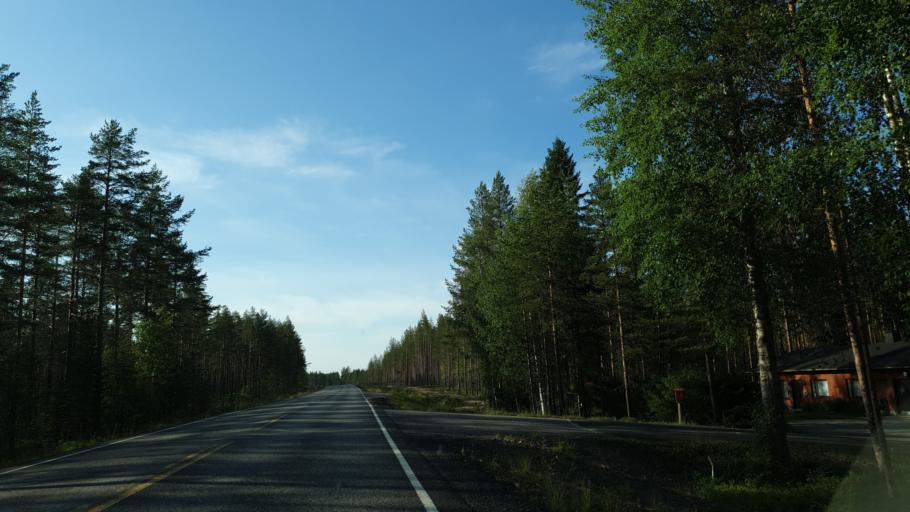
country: FI
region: Kainuu
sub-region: Kehys-Kainuu
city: Kuhmo
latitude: 64.0886
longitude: 29.4820
